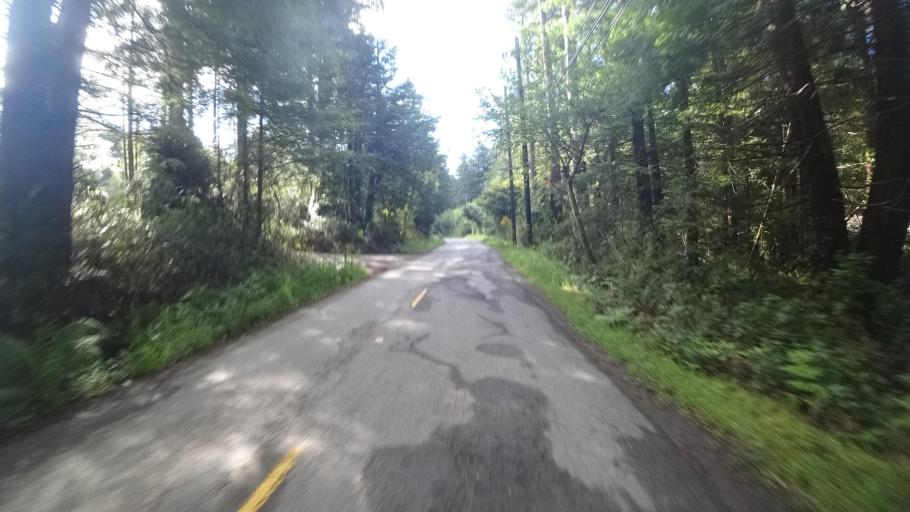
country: US
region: California
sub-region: Humboldt County
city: Westhaven-Moonstone
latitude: 41.0522
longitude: -124.1212
